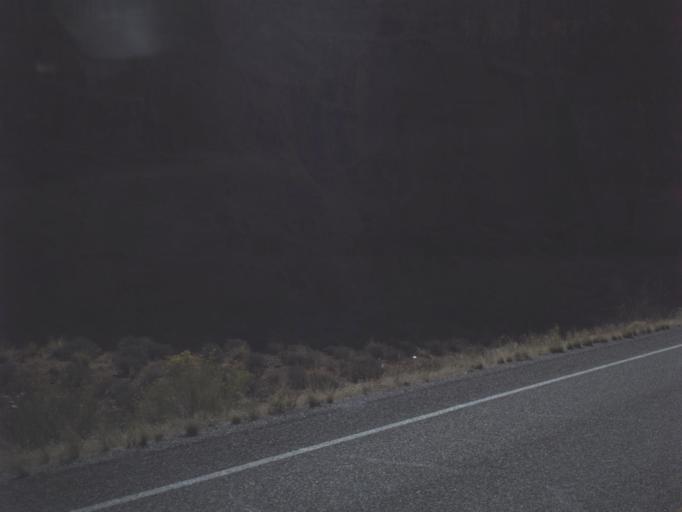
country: US
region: Utah
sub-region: San Juan County
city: Blanding
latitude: 37.9714
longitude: -110.4915
